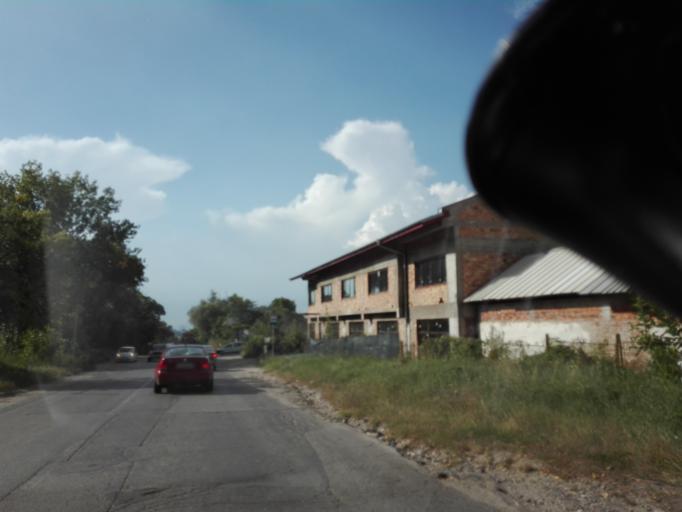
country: BG
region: Sofiya
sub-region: Obshtina Elin Pelin
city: Elin Pelin
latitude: 42.6140
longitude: 23.4610
